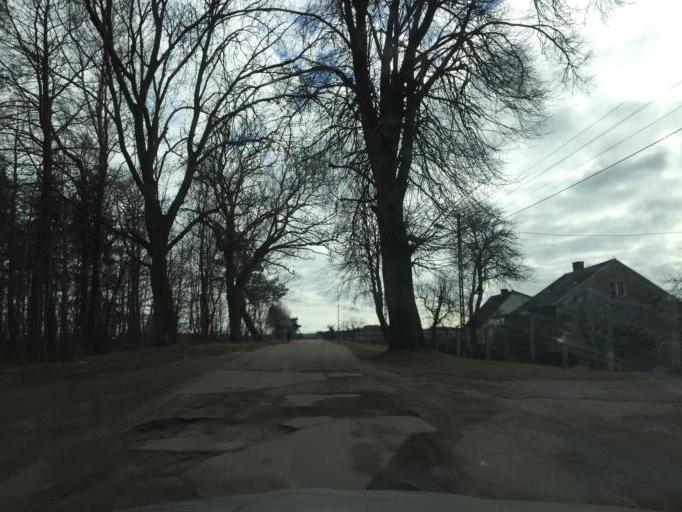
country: PL
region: Pomeranian Voivodeship
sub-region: Powiat kartuski
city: Banino
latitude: 54.3767
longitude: 18.4859
